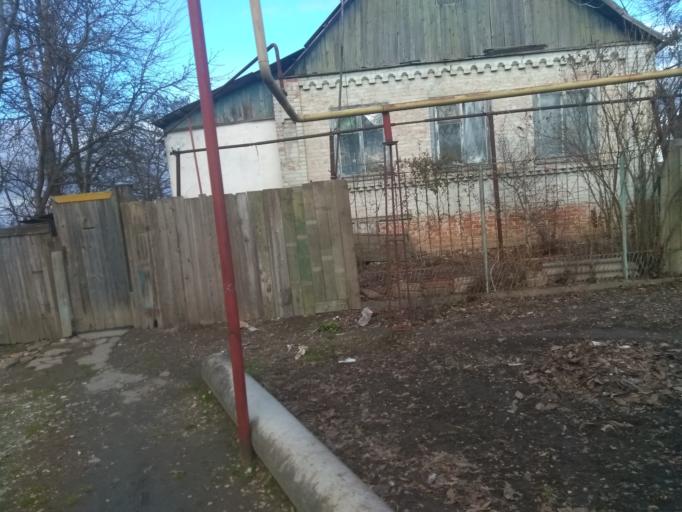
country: RU
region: Stavropol'skiy
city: Krasnokumskoye
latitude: 44.1782
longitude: 43.4796
